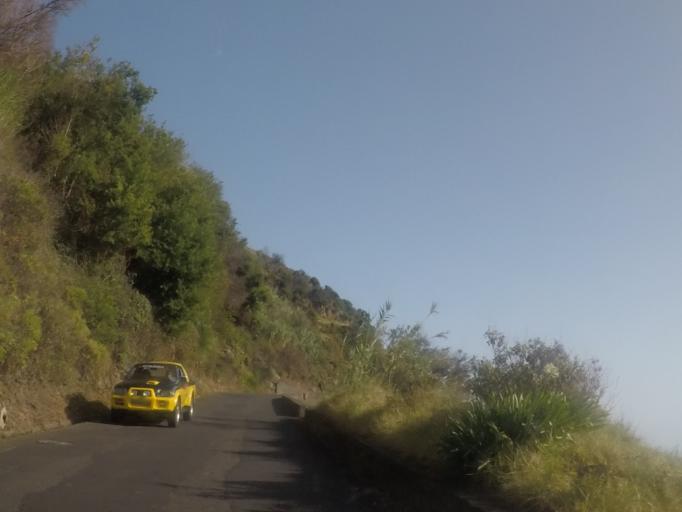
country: PT
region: Madeira
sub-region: Calheta
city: Arco da Calheta
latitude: 32.7102
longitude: -17.1303
